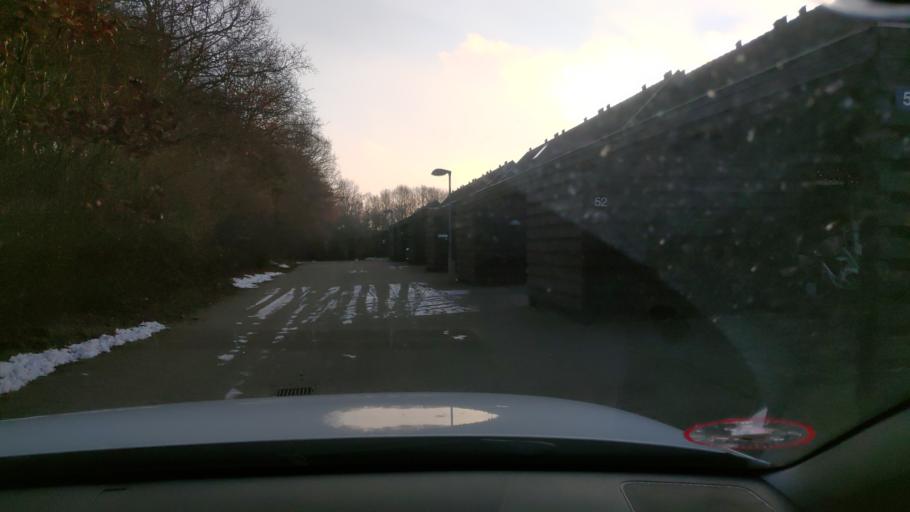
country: DK
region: Zealand
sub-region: Solrod Kommune
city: Solrod Strand
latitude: 55.5443
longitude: 12.2207
